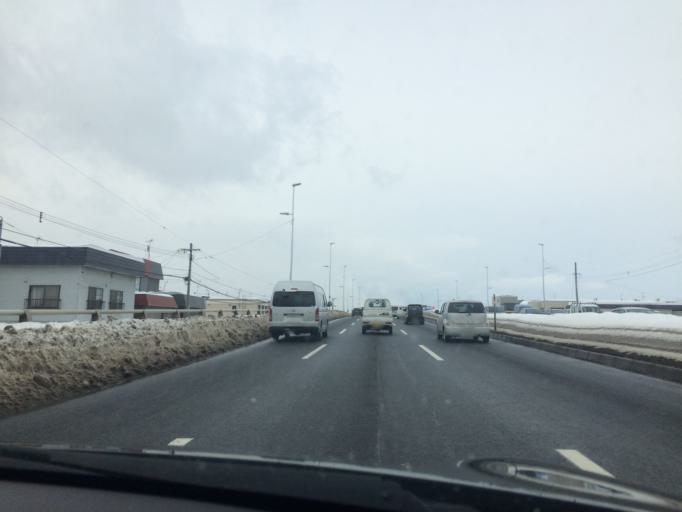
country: JP
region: Hokkaido
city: Sapporo
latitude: 43.0724
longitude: 141.4068
